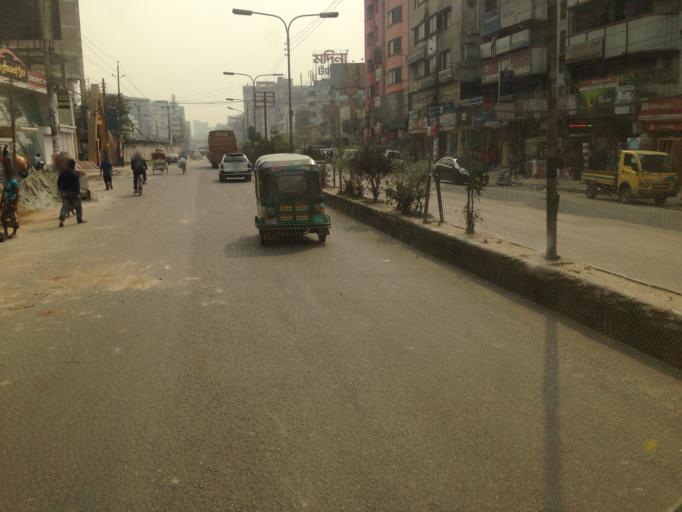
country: BD
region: Dhaka
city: Tungi
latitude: 23.8152
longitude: 90.4212
